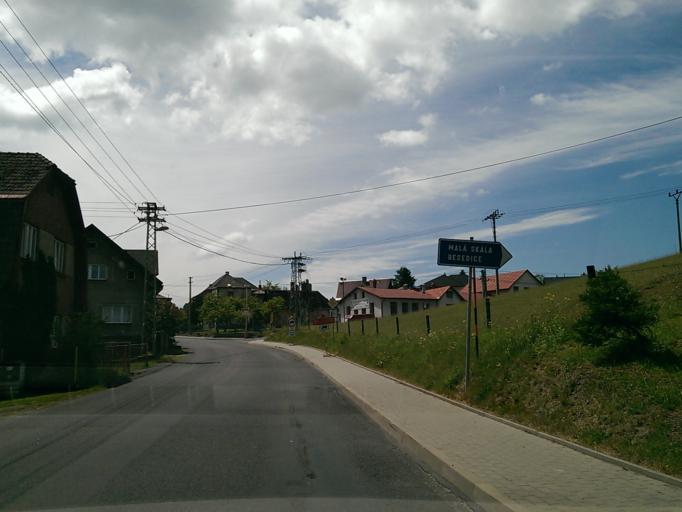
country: CZ
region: Liberecky
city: Zelezny Brod
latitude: 50.6252
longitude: 15.2287
